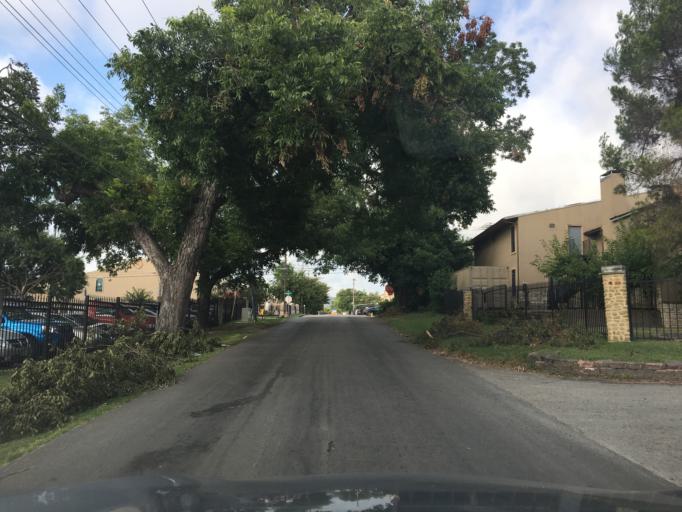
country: US
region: Texas
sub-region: Dallas County
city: University Park
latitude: 32.8796
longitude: -96.7540
